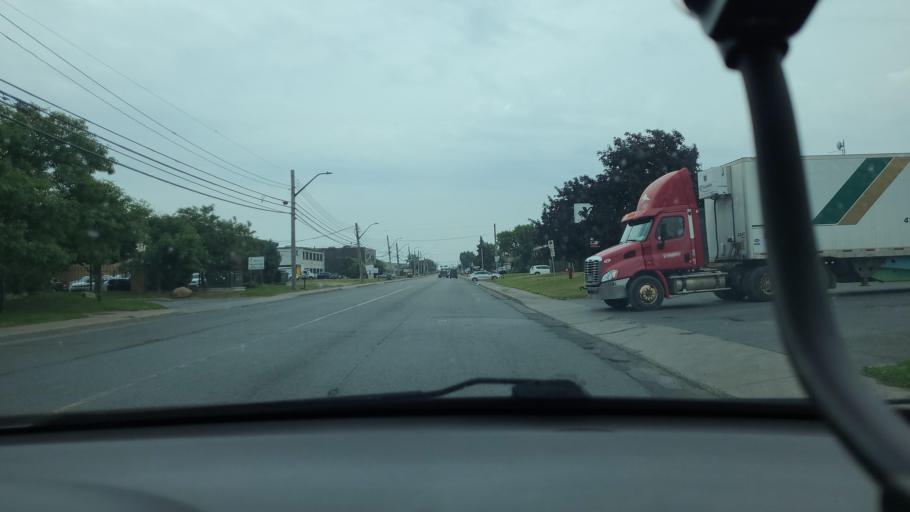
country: CA
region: Quebec
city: Hampstead
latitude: 45.4833
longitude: -73.7132
